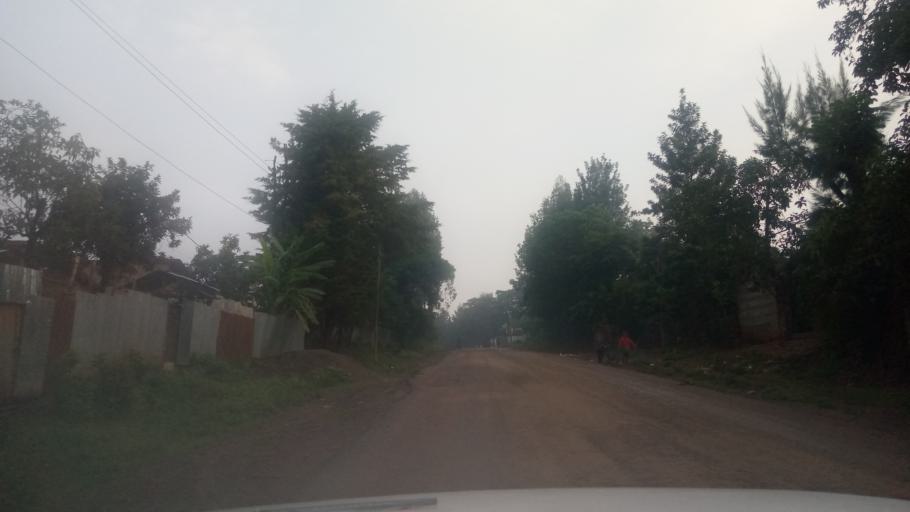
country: ET
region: Oromiya
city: Jima
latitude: 7.6973
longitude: 36.8158
